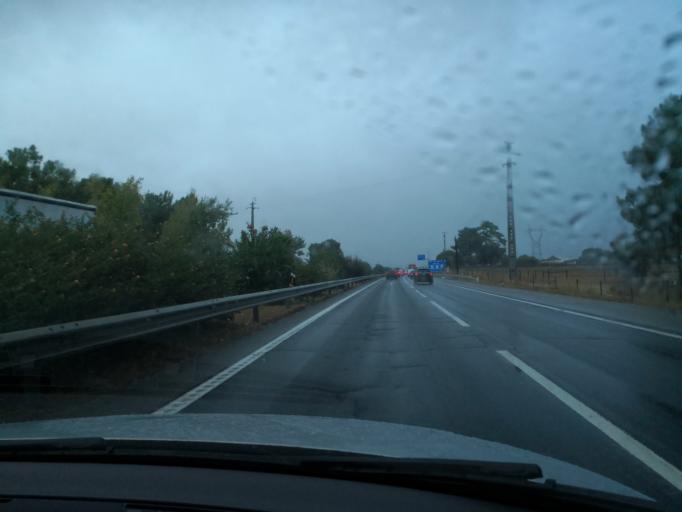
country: PT
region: Setubal
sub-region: Moita
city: Moita
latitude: 38.6602
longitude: -8.9609
